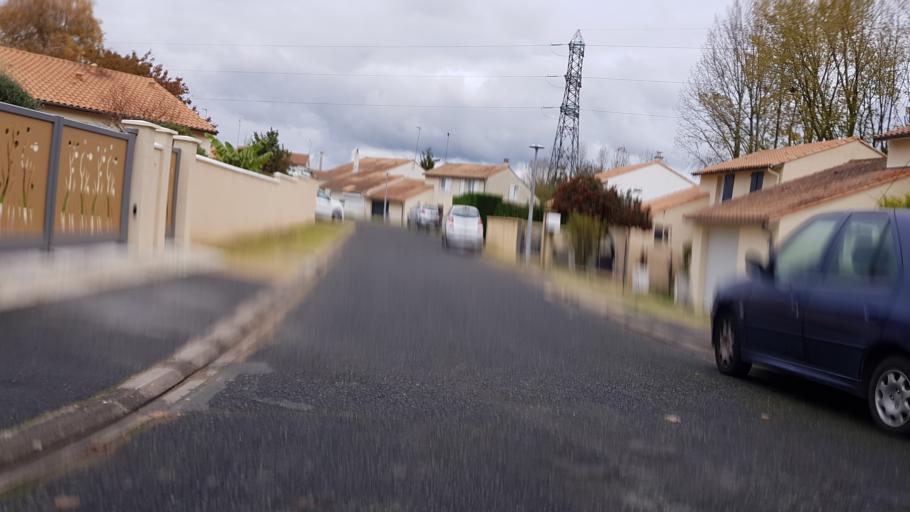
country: FR
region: Poitou-Charentes
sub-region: Departement de la Vienne
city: Chasseneuil-du-Poitou
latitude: 46.6575
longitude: 0.3827
